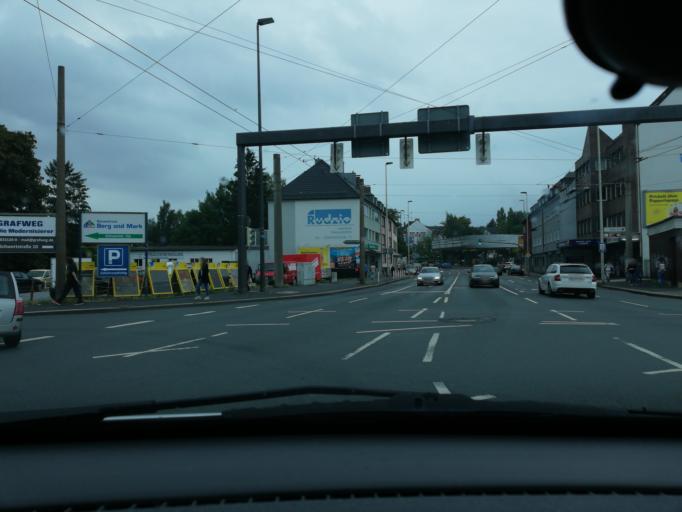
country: DE
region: North Rhine-Westphalia
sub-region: Regierungsbezirk Dusseldorf
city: Solingen
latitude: 51.1670
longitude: 7.0882
